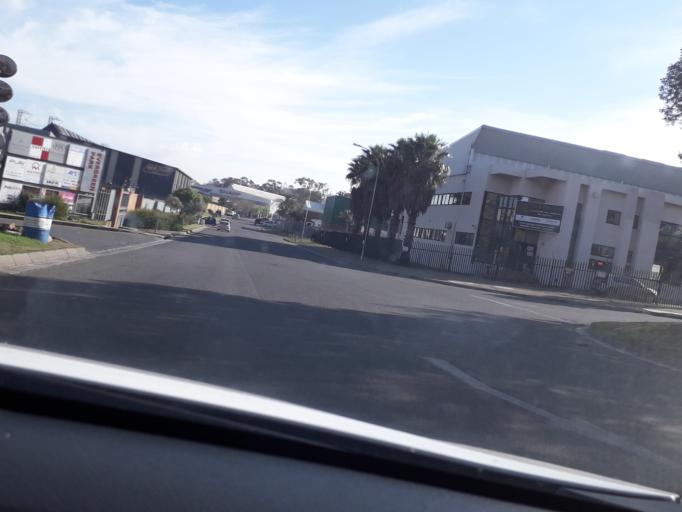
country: ZA
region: Gauteng
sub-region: City of Johannesburg Metropolitan Municipality
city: Modderfontein
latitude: -26.1604
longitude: 28.1827
